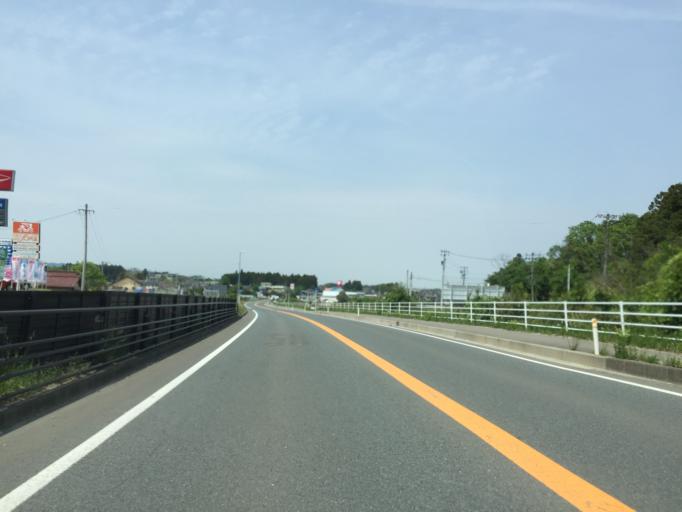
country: JP
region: Miyagi
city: Marumori
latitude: 37.8649
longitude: 140.9206
